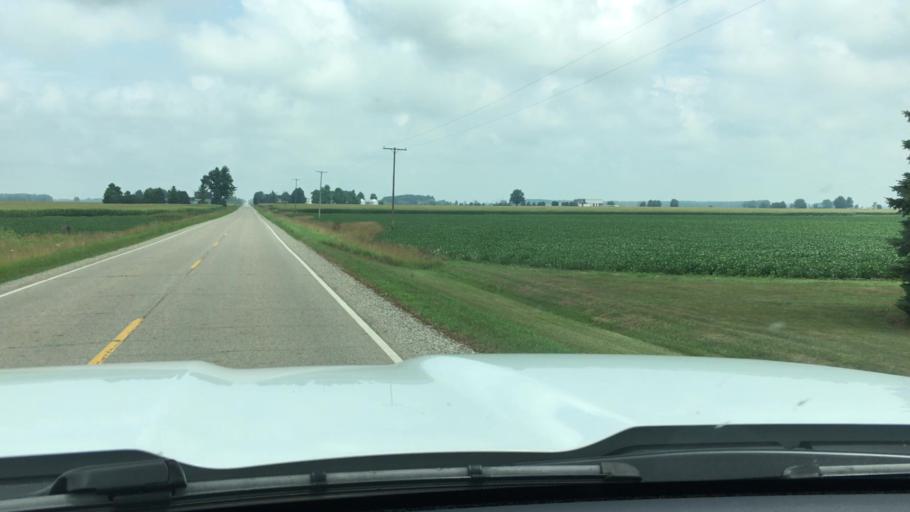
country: US
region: Michigan
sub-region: Sanilac County
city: Marlette
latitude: 43.3769
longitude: -83.0064
